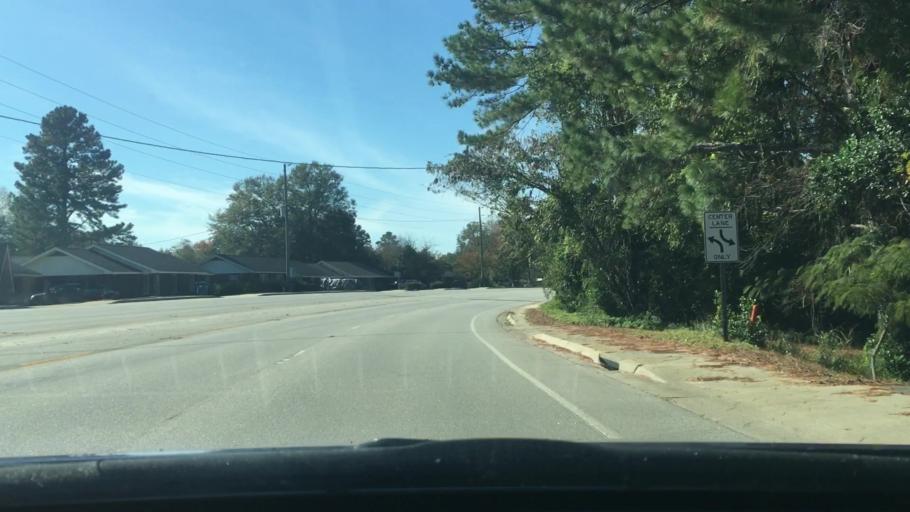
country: US
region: South Carolina
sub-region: Sumter County
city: Cane Savannah
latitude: 33.8978
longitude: -80.3988
